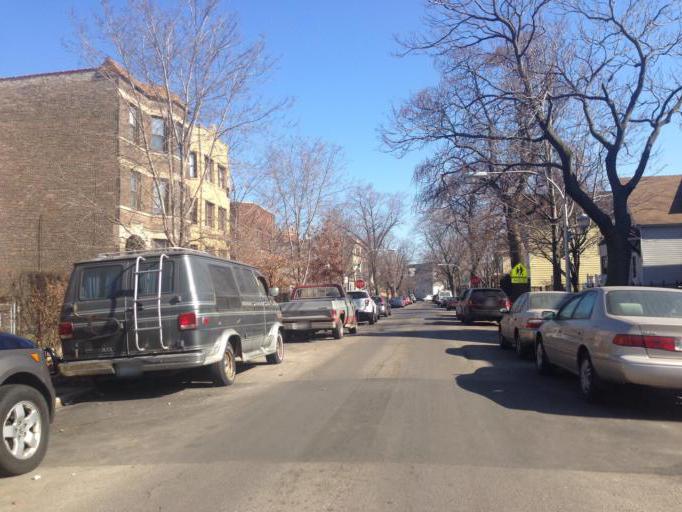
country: US
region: Illinois
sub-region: Cook County
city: Lincolnwood
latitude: 41.9376
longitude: -87.7023
